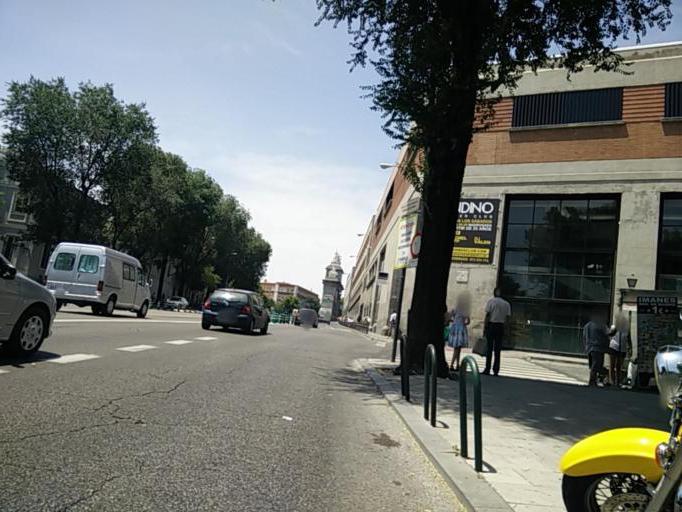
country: ES
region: Madrid
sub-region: Provincia de Madrid
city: Madrid
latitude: 40.4062
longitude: -3.7093
